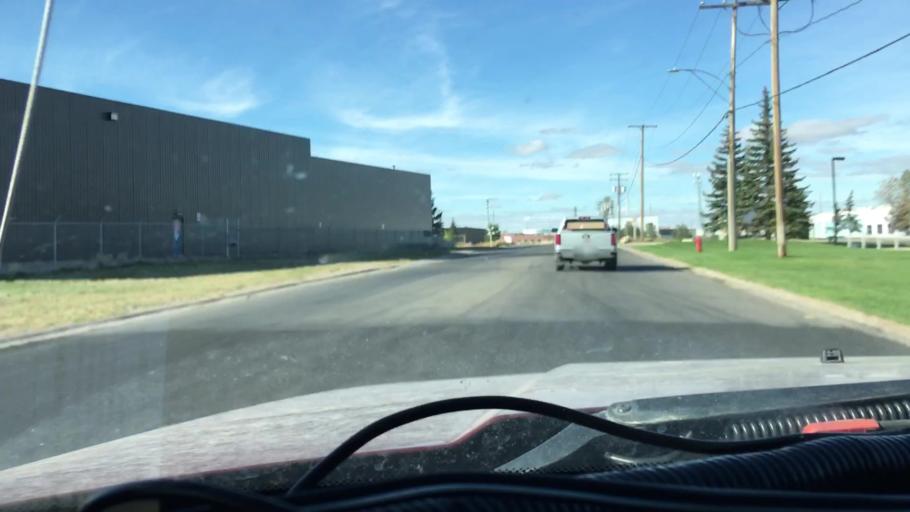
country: CA
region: Saskatchewan
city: Regina
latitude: 50.4757
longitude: -104.5615
